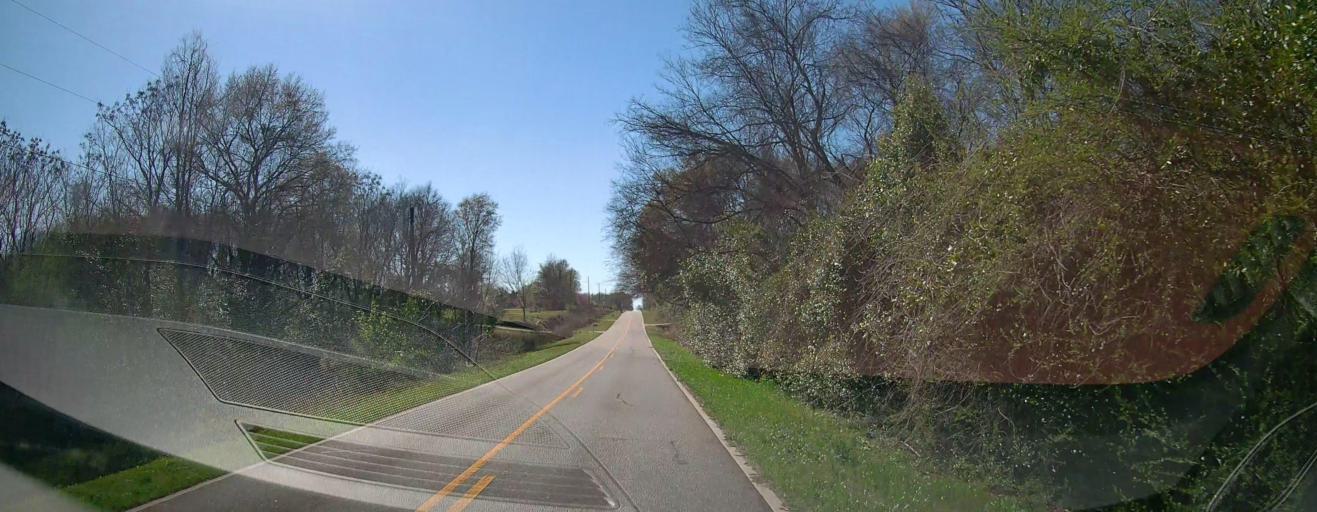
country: US
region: Georgia
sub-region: Peach County
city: Byron
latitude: 32.6447
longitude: -83.7950
